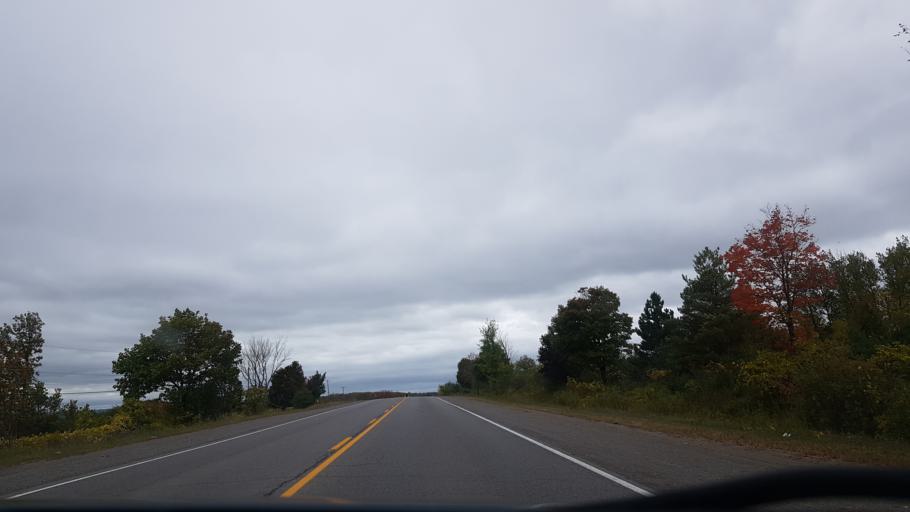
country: CA
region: Ontario
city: Peterborough
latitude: 44.2613
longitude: -78.3769
